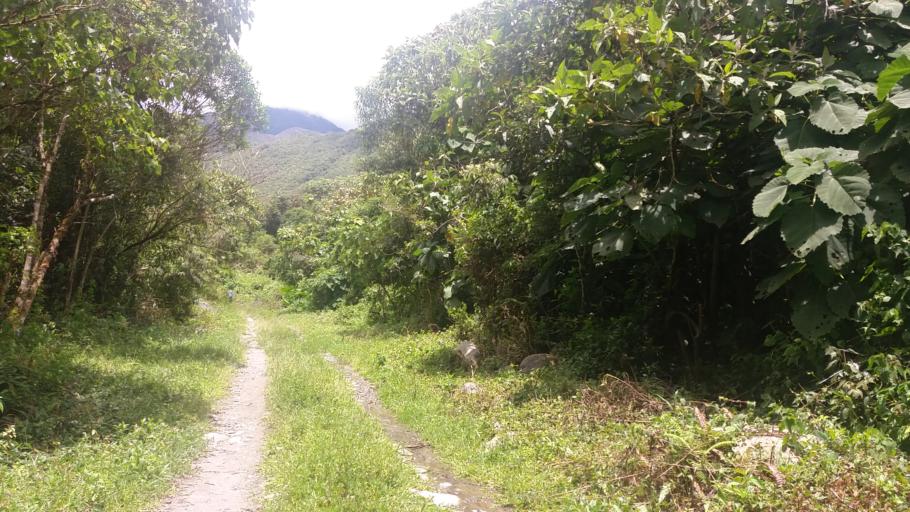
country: BO
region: Cochabamba
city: Colomi
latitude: -17.0858
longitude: -66.0104
